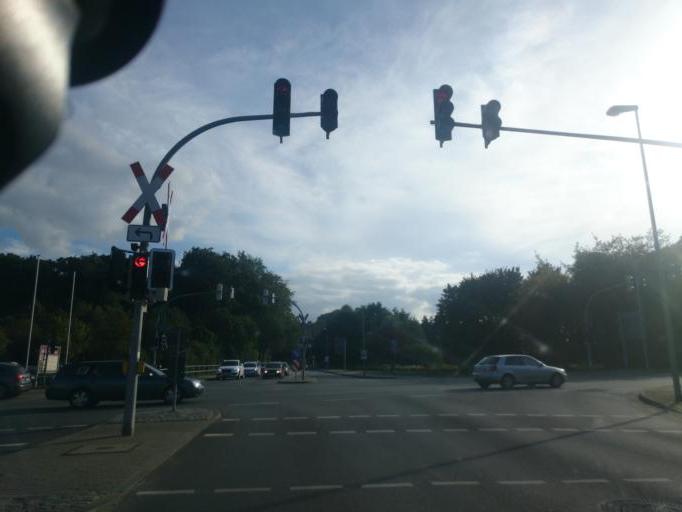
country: DE
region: Mecklenburg-Vorpommern
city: Bad Doberan
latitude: 54.1033
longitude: 11.9024
